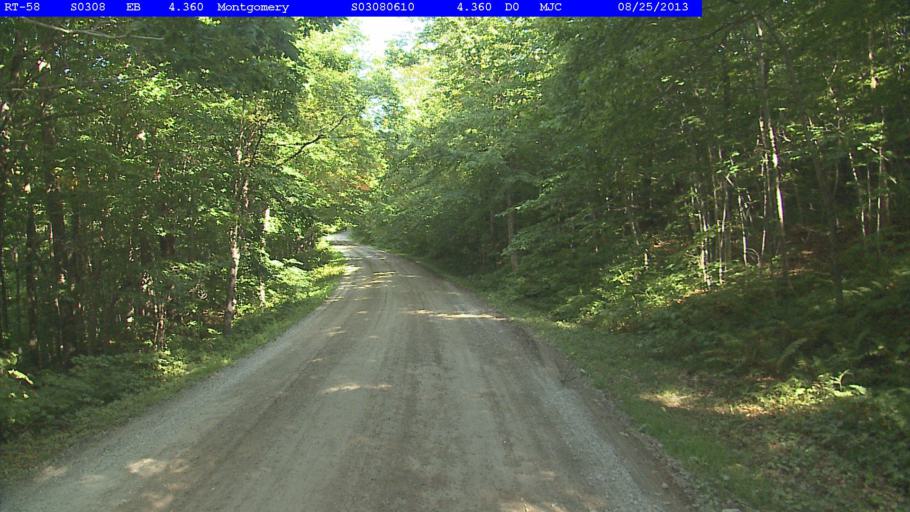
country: US
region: Vermont
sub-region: Franklin County
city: Richford
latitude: 44.8442
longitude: -72.5405
